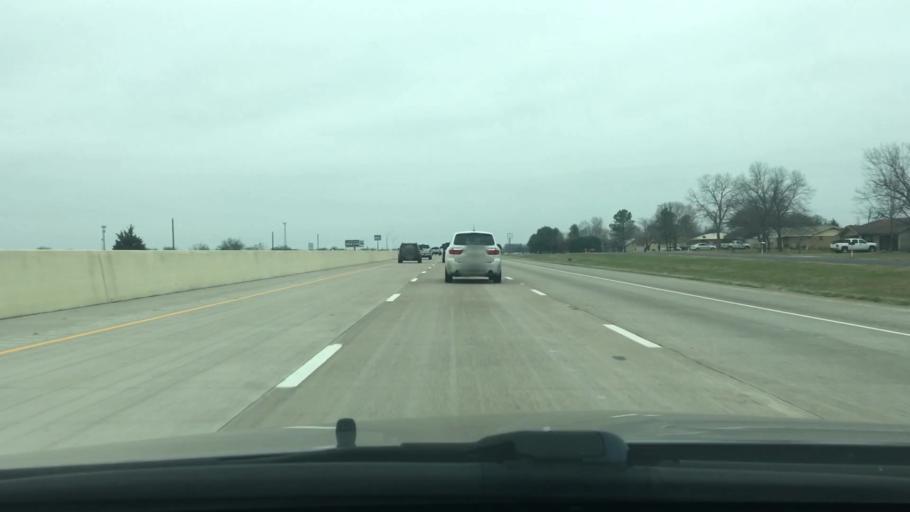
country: US
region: Texas
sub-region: Navarro County
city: Corsicana
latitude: 32.0164
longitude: -96.4373
